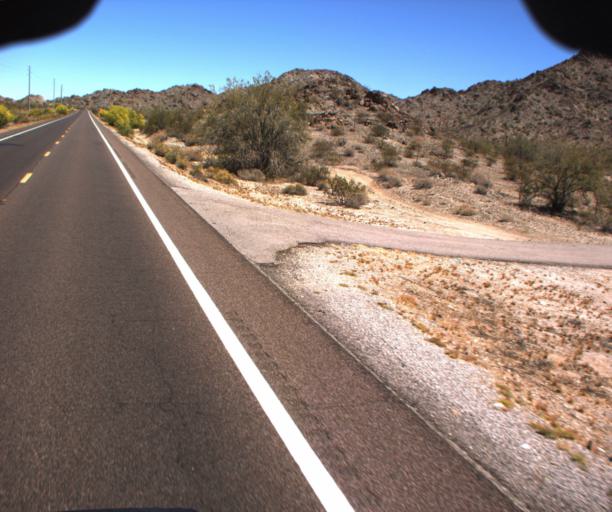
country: US
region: Arizona
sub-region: La Paz County
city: Salome
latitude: 33.7319
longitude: -113.6798
